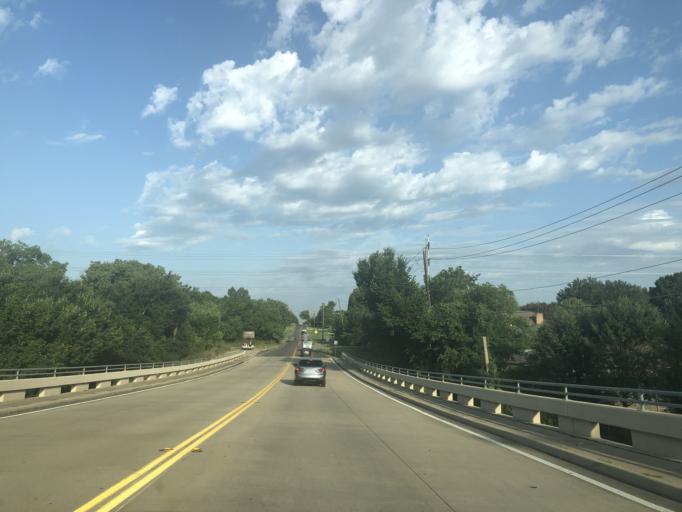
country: US
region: Texas
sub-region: Dallas County
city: Grand Prairie
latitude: 32.7654
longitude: -97.0305
